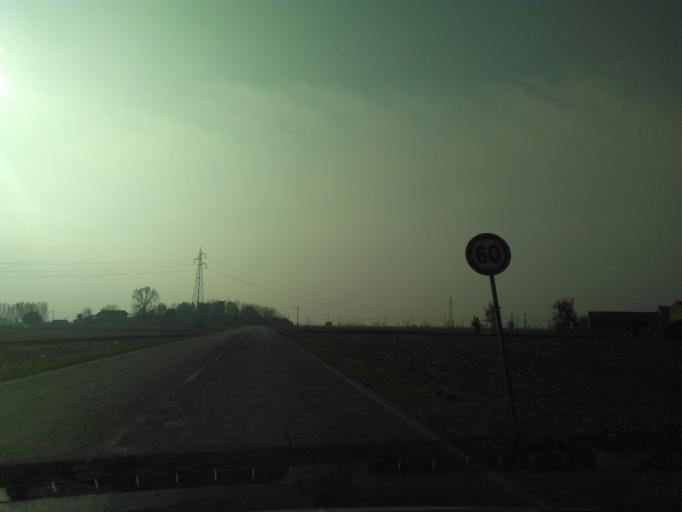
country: IT
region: Piedmont
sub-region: Provincia di Vercelli
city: Livorno Ferraris
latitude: 45.2795
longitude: 8.0909
